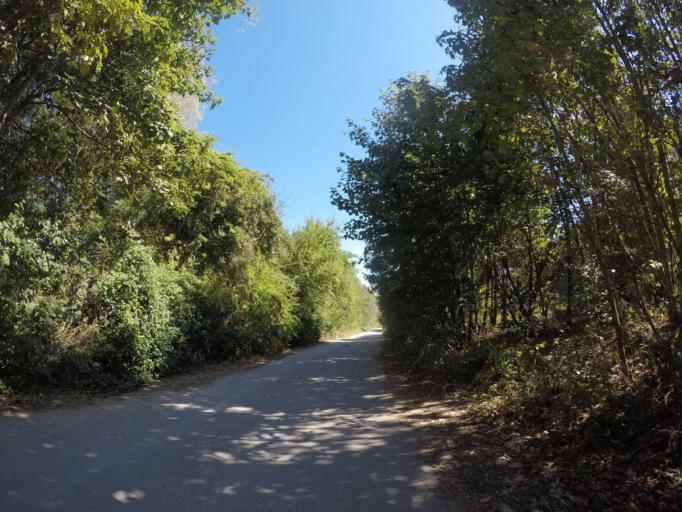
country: DE
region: Bavaria
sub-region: Swabia
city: Senden
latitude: 48.3558
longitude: 10.0478
